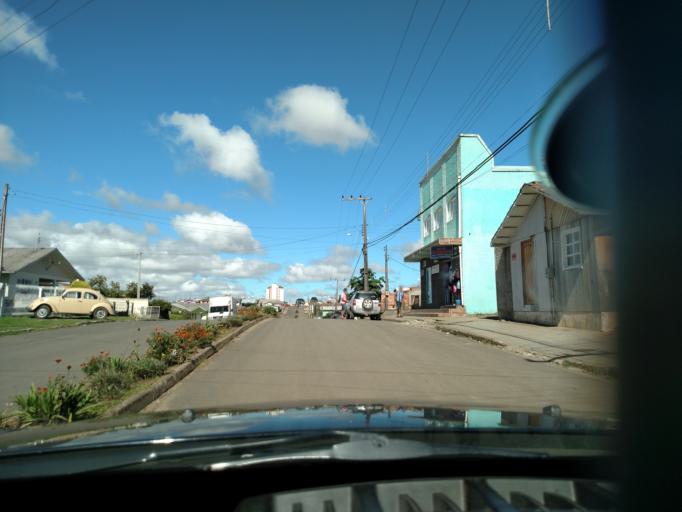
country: BR
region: Santa Catarina
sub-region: Sao Joaquim
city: Sao Joaquim
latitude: -28.2903
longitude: -49.9237
